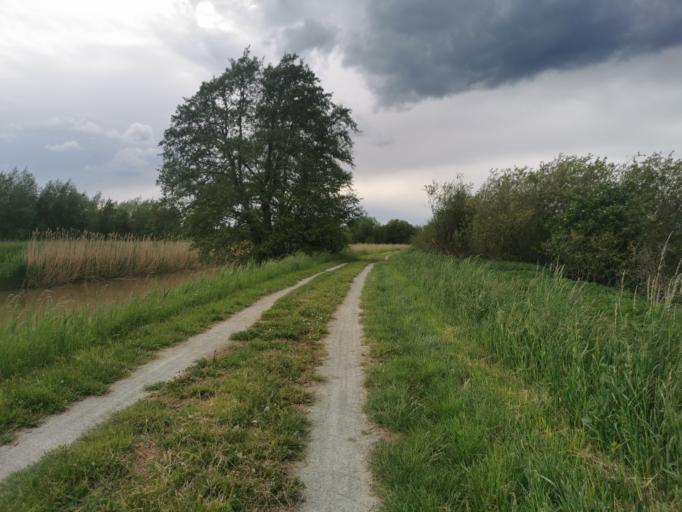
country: SK
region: Trnavsky
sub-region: Okres Skalica
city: Skalica
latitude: 48.8708
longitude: 17.2181
